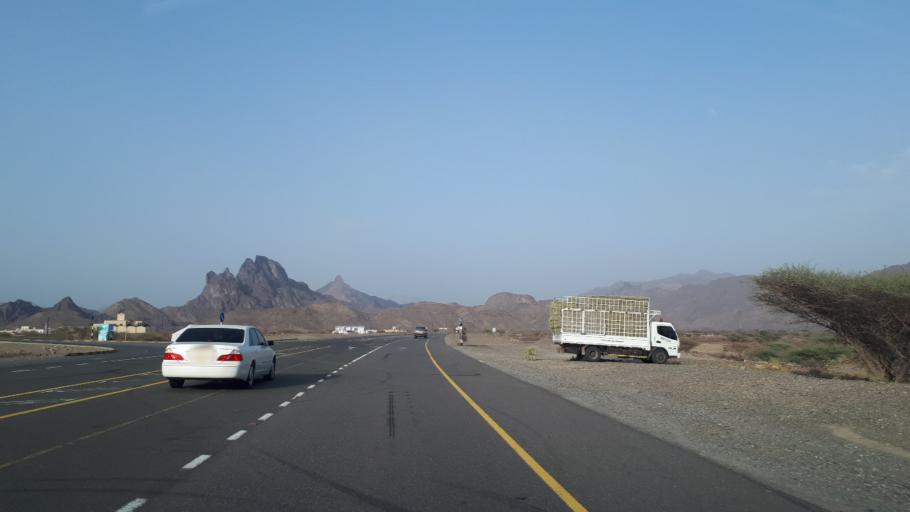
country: OM
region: Az Zahirah
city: Yanqul
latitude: 23.4970
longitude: 56.8485
